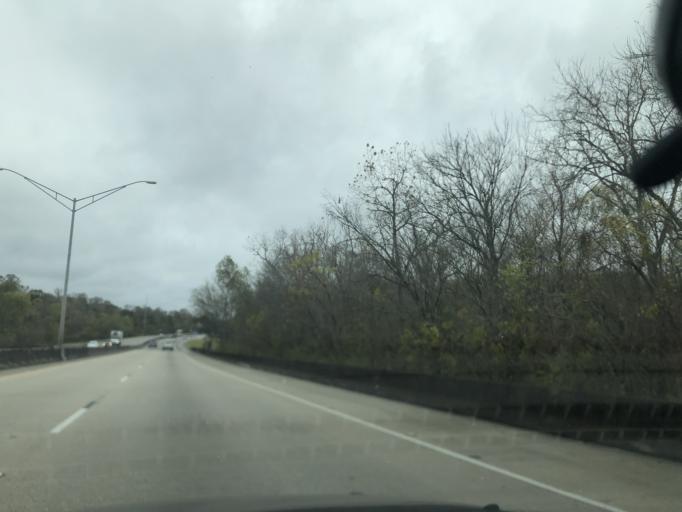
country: US
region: Louisiana
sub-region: Saint Charles Parish
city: Destrehan
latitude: 29.9560
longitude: -90.3662
